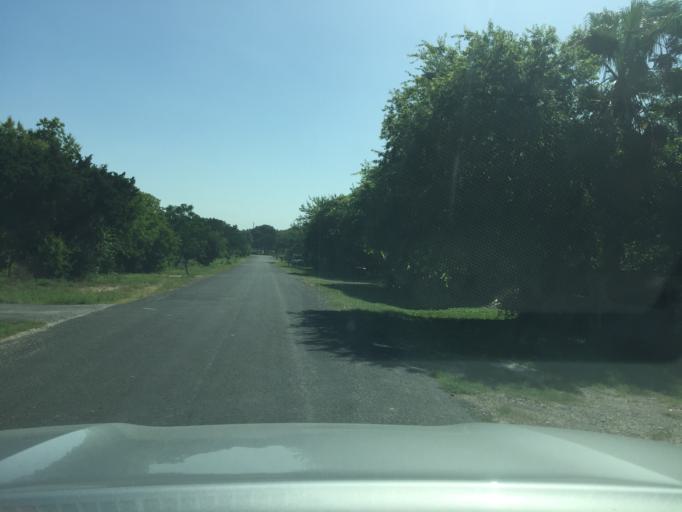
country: US
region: Texas
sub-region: Bexar County
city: Timberwood Park
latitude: 29.7052
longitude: -98.4790
